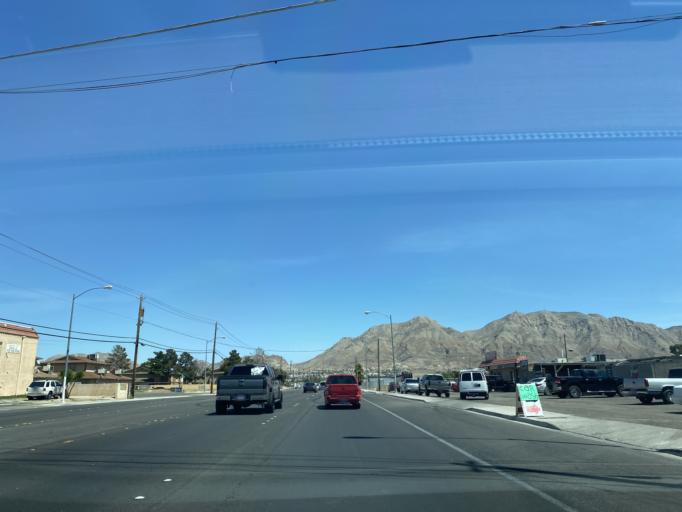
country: US
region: Nevada
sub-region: Clark County
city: Sunrise Manor
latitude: 36.1962
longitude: -115.0568
